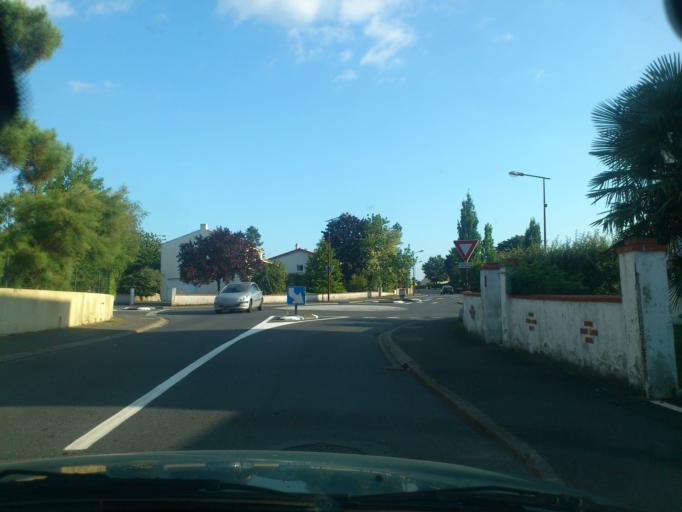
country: FR
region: Pays de la Loire
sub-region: Departement de la Loire-Atlantique
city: Saint-Hilaire-de-Clisson
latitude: 47.0607
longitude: -1.3096
